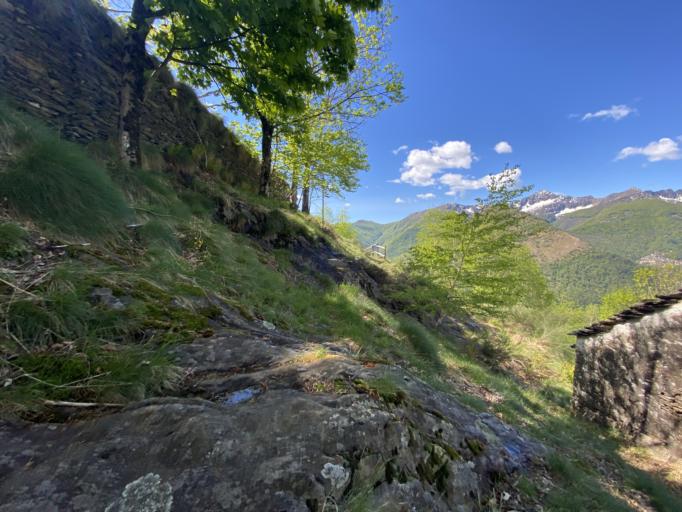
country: IT
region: Piedmont
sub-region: Provincia Verbano-Cusio-Ossola
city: Falmenta
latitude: 46.1028
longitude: 8.6028
